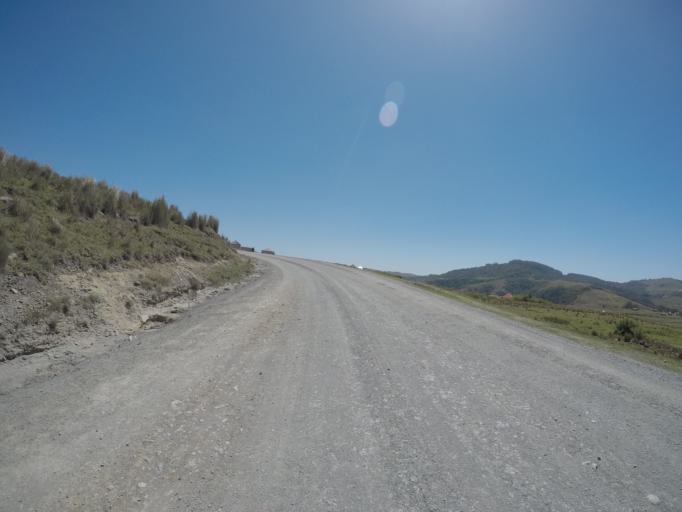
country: ZA
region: Eastern Cape
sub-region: OR Tambo District Municipality
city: Libode
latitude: -32.0176
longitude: 29.0805
